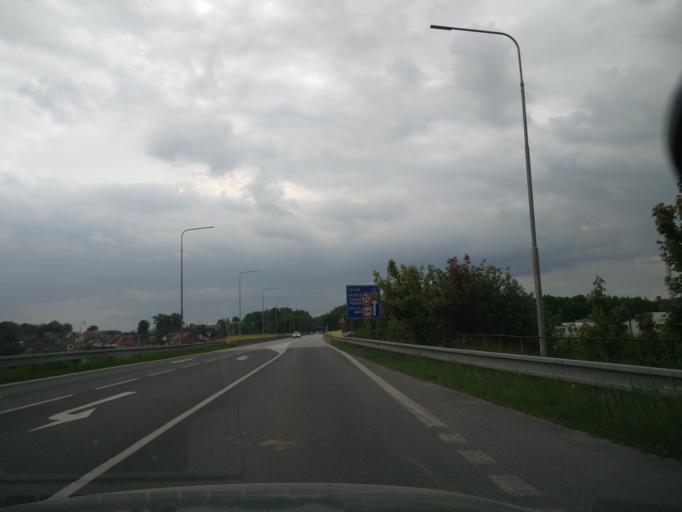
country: CZ
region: Jihocesky
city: Protivin
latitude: 49.2124
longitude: 14.2165
